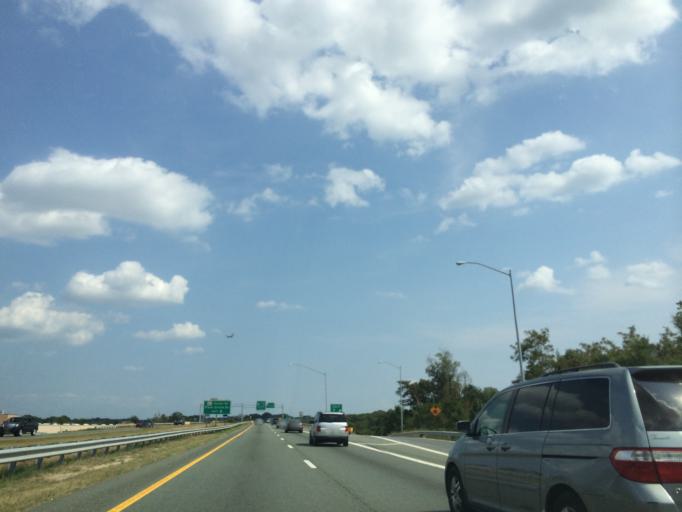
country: US
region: Maryland
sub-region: Howard County
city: Hanover
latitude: 39.1844
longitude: -76.7493
